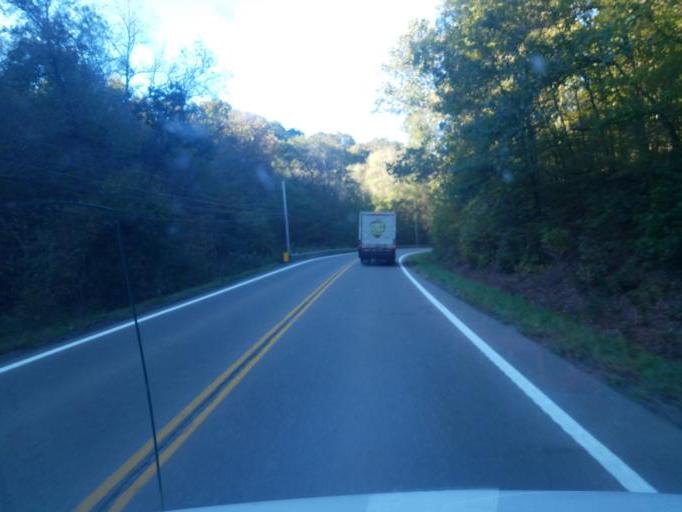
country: US
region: Ohio
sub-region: Columbiana County
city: New Waterford
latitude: 40.7763
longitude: -80.6277
